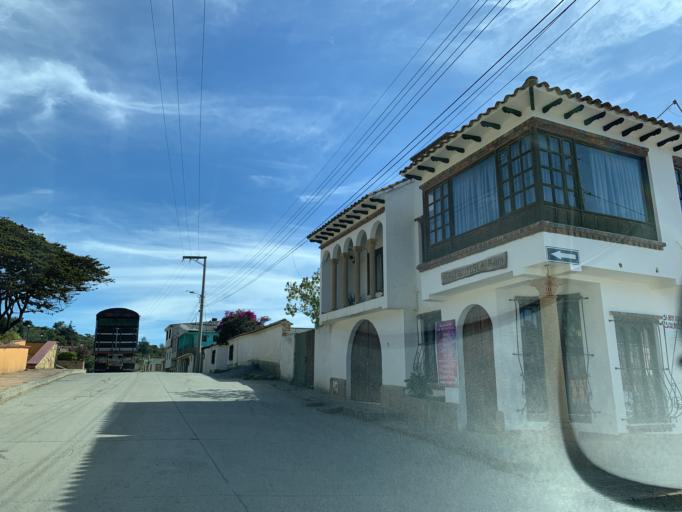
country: CO
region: Boyaca
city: Santa Sofia
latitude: 5.7131
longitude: -73.6036
